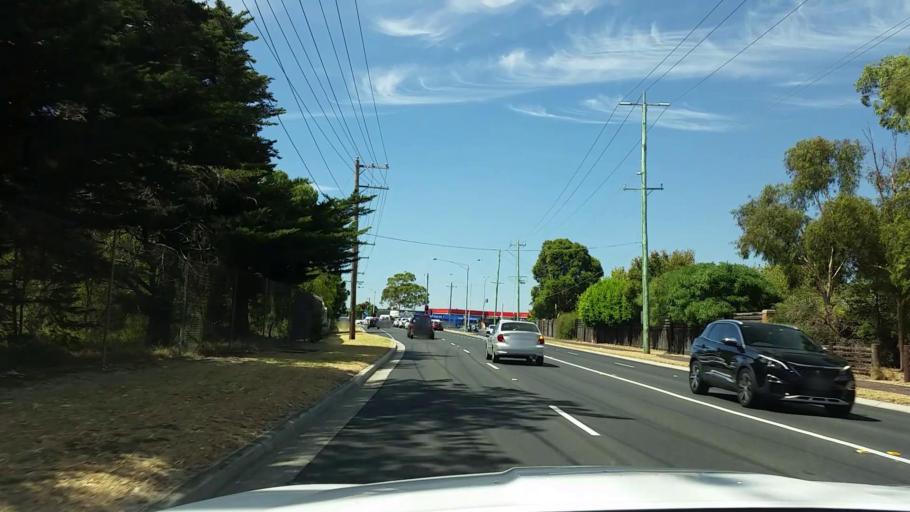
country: AU
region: Victoria
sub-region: Kingston
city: Mordialloc
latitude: -38.0006
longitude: 145.1033
